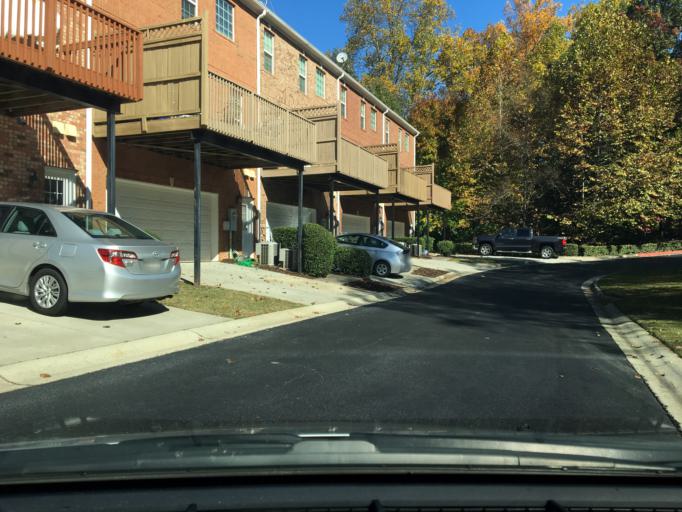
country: US
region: Georgia
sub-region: Fulton County
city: Johns Creek
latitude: 34.0467
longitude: -84.1819
